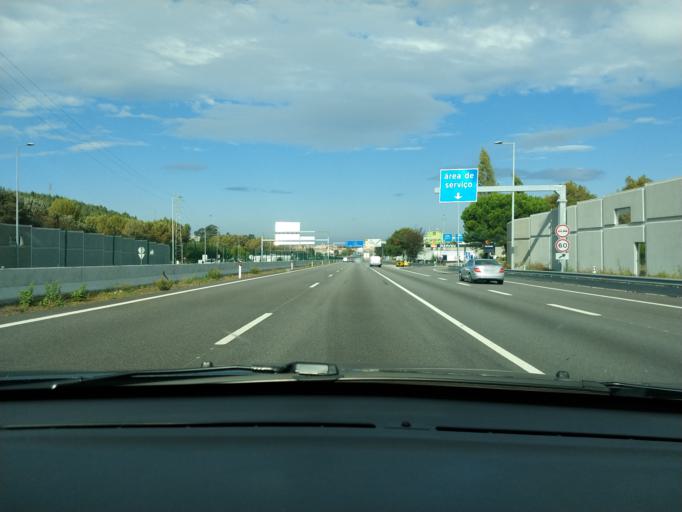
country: PT
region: Porto
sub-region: Vila Nova de Gaia
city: Vilar de Andorinho
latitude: 41.0998
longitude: -8.5963
